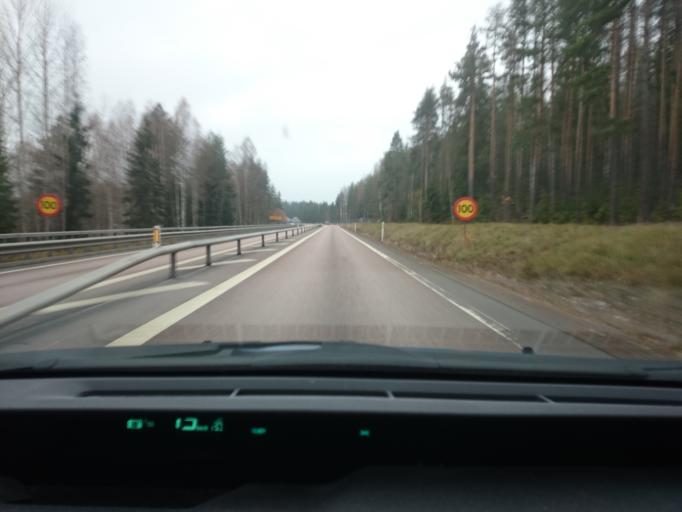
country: SE
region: Dalarna
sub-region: Avesta Kommun
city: Avesta
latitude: 60.1896
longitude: 16.1173
